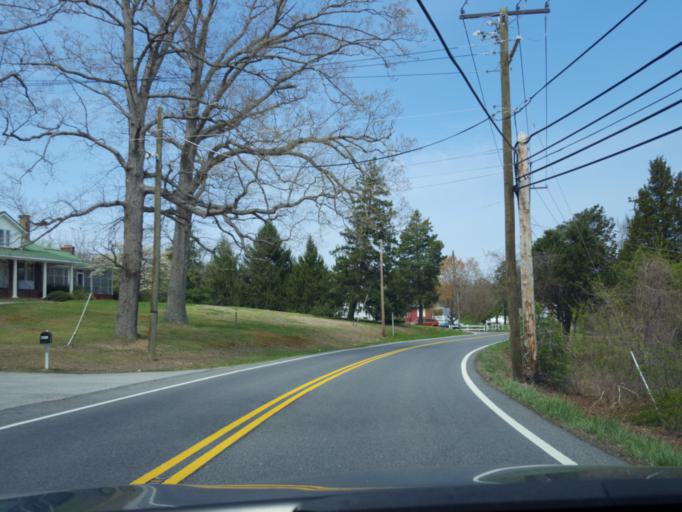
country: US
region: Maryland
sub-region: Prince George's County
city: Croom
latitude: 38.7534
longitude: -76.7643
